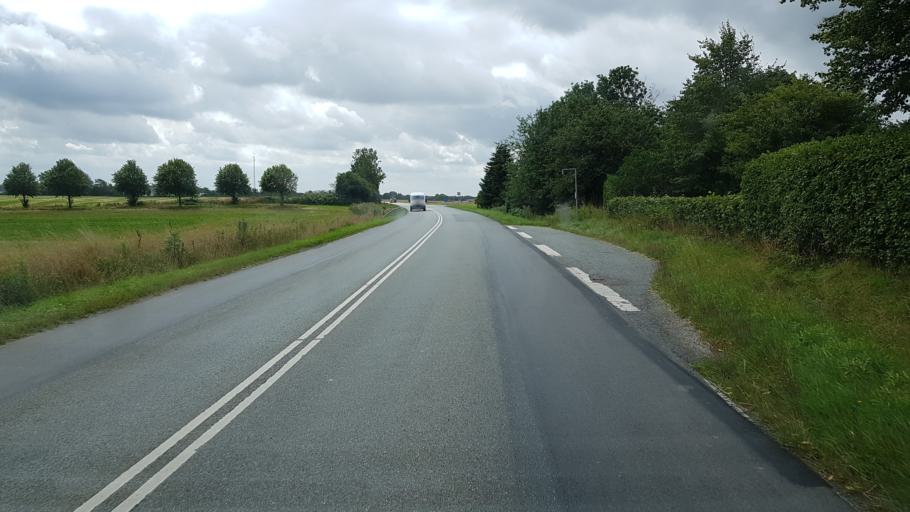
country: DK
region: South Denmark
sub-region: Kolding Kommune
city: Lunderskov
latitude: 55.4645
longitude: 9.3838
